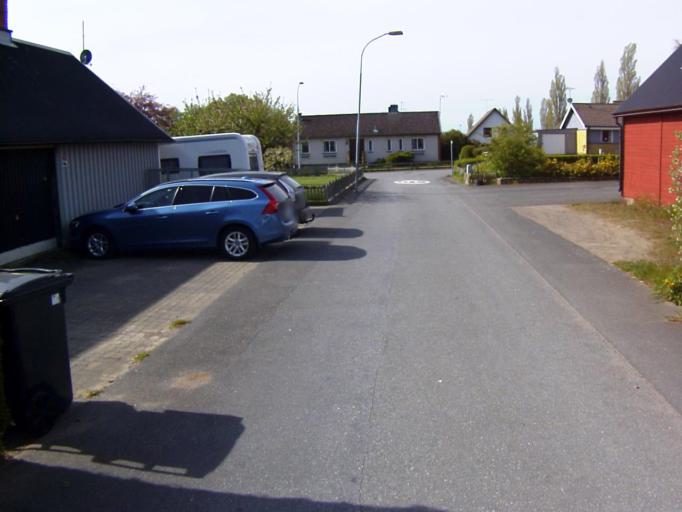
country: SE
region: Skane
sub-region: Kristianstads Kommun
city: Fjalkinge
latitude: 56.0403
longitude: 14.2745
